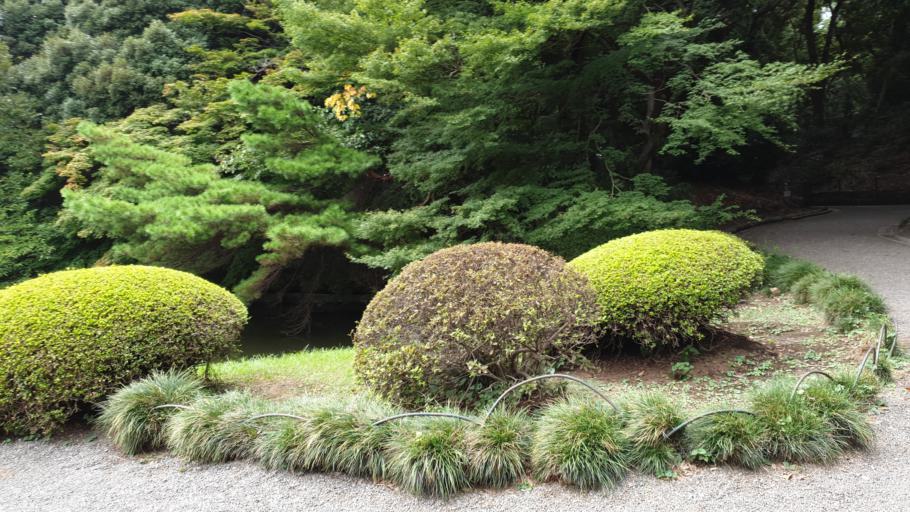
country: JP
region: Tokyo
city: Tokyo
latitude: 35.6861
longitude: 139.7060
